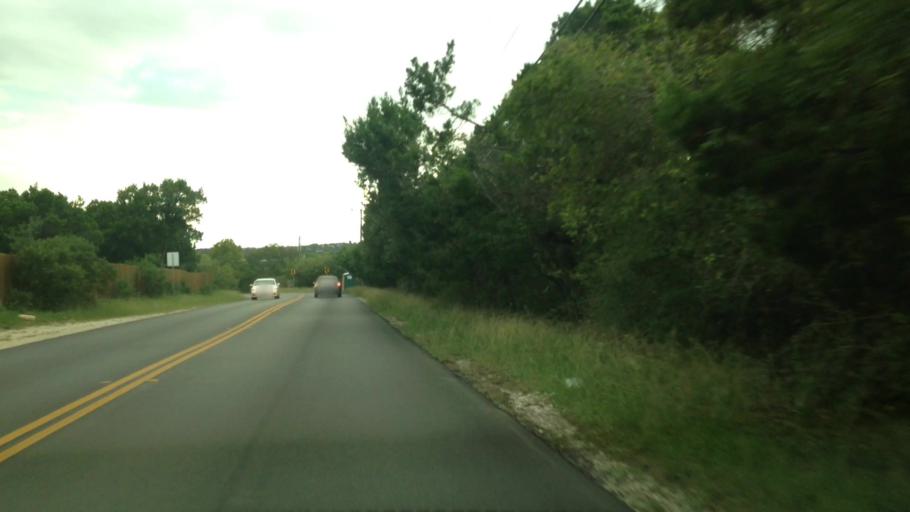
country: US
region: Texas
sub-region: Bexar County
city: Cross Mountain
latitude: 29.6315
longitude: -98.6033
